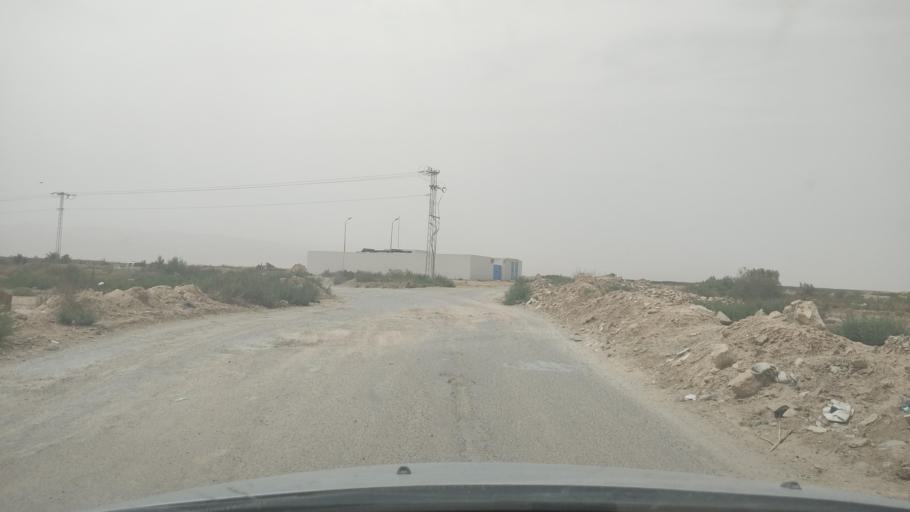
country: TN
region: Gafsa
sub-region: Gafsa Municipality
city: Gafsa
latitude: 34.3257
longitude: 8.9513
